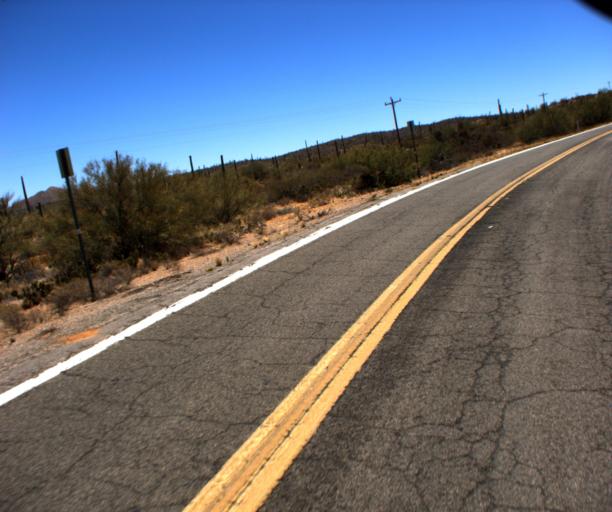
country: US
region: Arizona
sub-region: Pima County
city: Sells
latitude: 32.1767
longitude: -112.1913
